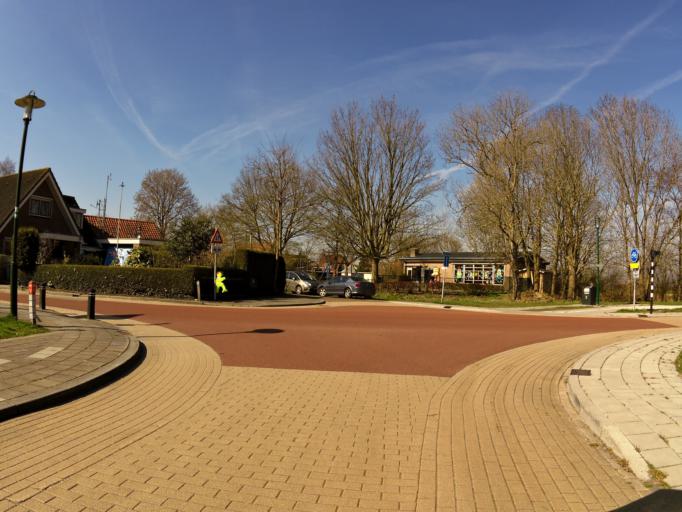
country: NL
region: Overijssel
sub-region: Gemeente Steenwijkerland
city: Oldemarkt
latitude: 52.8095
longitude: 5.9212
